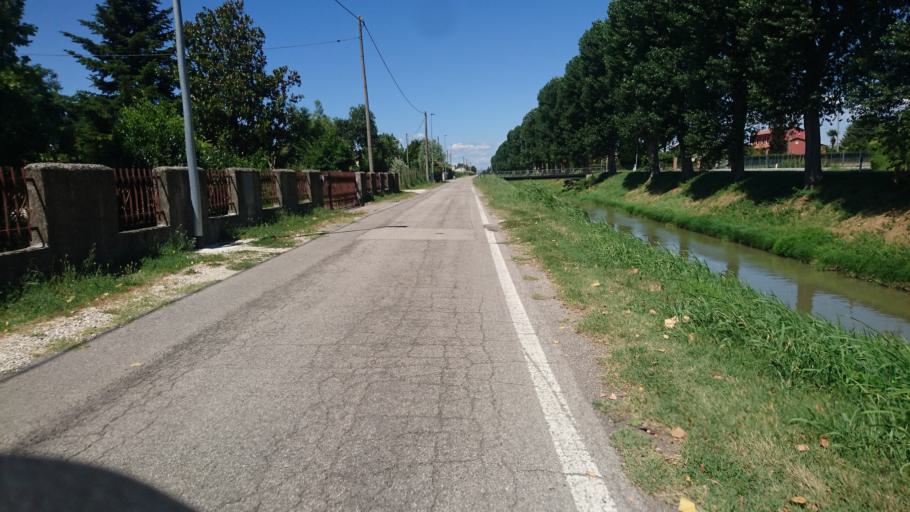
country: IT
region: Veneto
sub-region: Provincia di Padova
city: Sant'Angelo di Piove di Sacco
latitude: 45.3041
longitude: 12.0078
